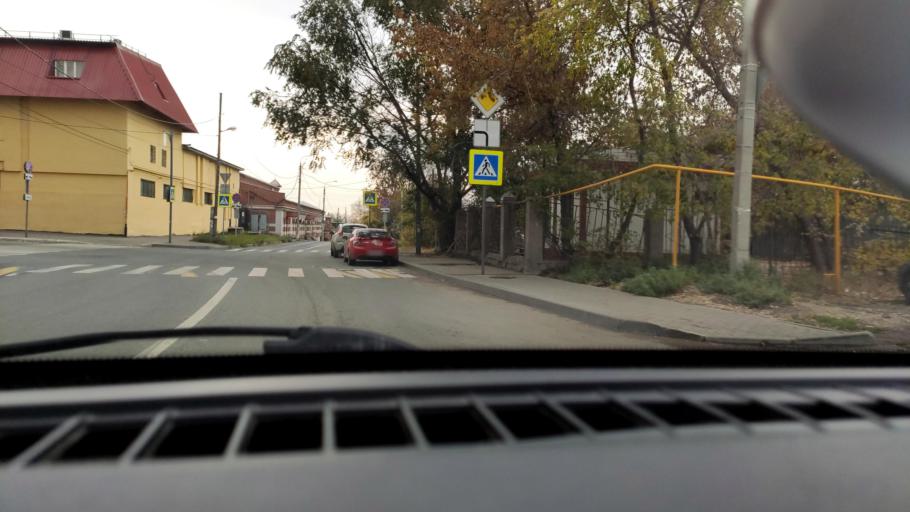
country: RU
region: Samara
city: Samara
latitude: 53.1812
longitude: 50.0941
